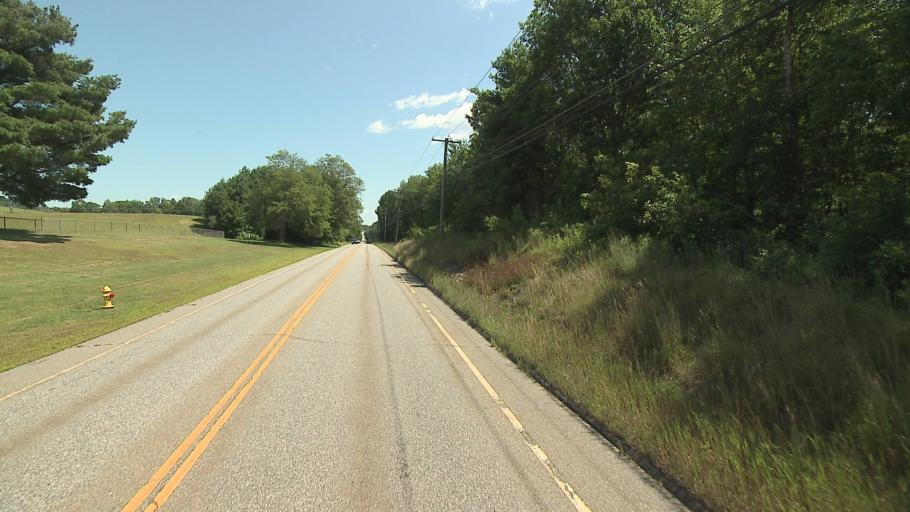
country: US
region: Connecticut
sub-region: Hartford County
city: Collinsville
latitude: 41.7781
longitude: -72.9880
